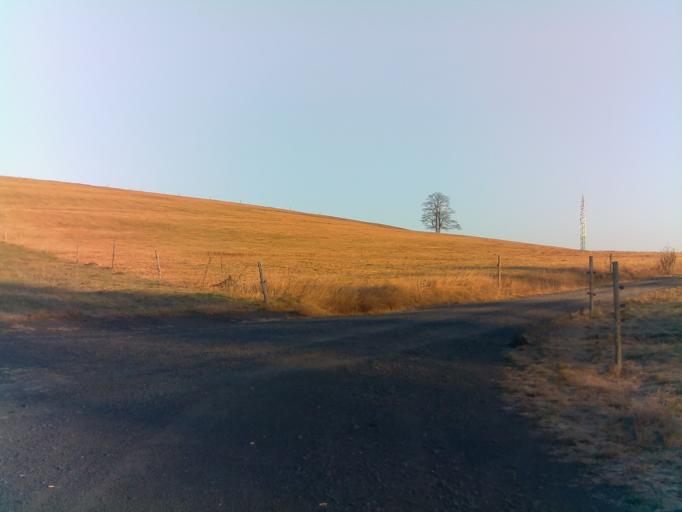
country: DE
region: Thuringia
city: Judenbach
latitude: 50.3818
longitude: 11.2109
